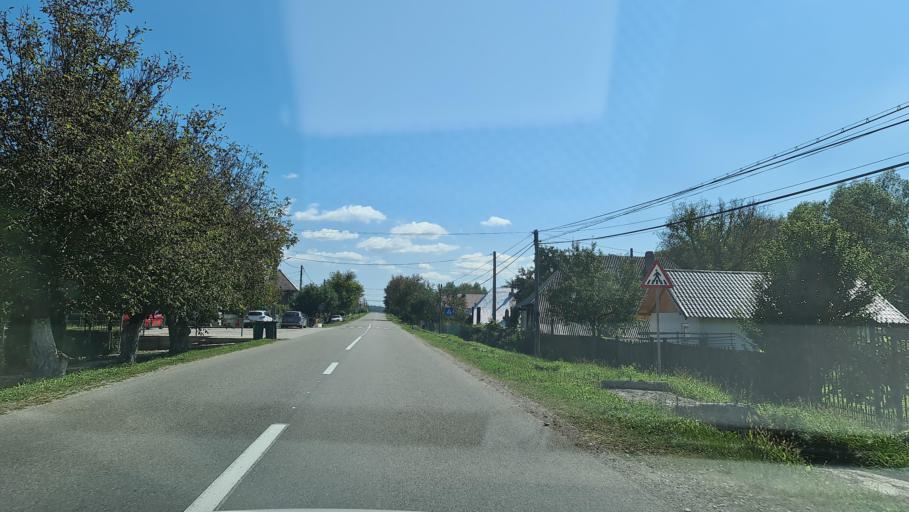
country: RO
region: Bacau
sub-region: Comuna Balcani
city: Frumoasa
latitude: 46.6583
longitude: 26.5477
